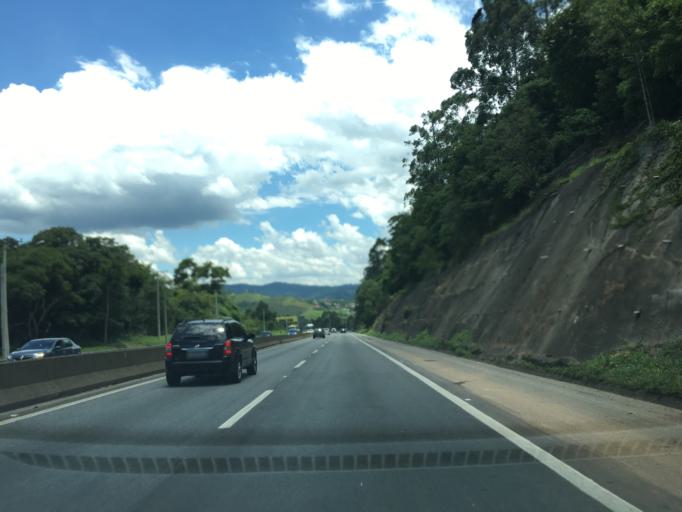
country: BR
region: Sao Paulo
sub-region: Mairipora
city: Mairipora
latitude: -23.2973
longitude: -46.5717
